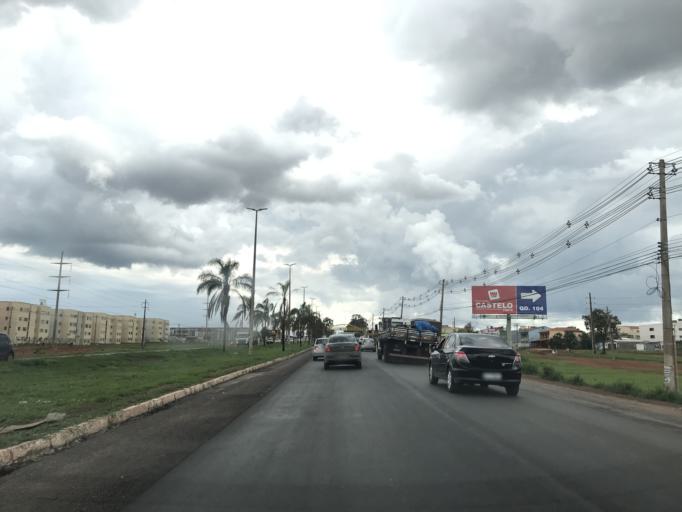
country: BR
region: Federal District
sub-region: Brasilia
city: Brasilia
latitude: -15.8962
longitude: -48.0560
